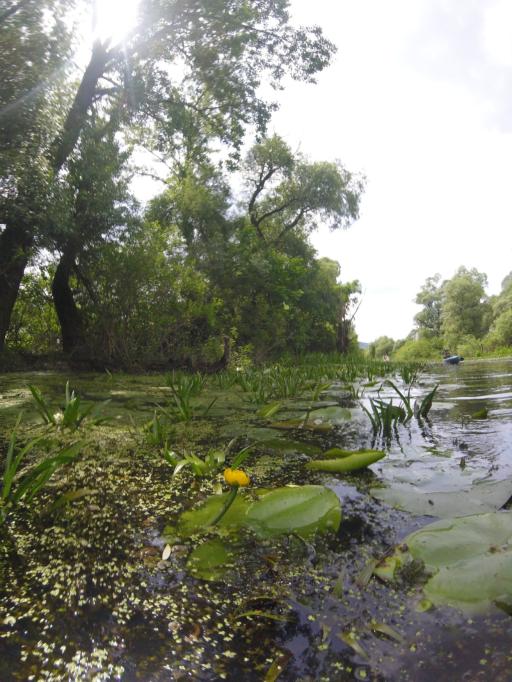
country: HU
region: Borsod-Abauj-Zemplen
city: Tokaj
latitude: 48.1541
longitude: 21.4241
